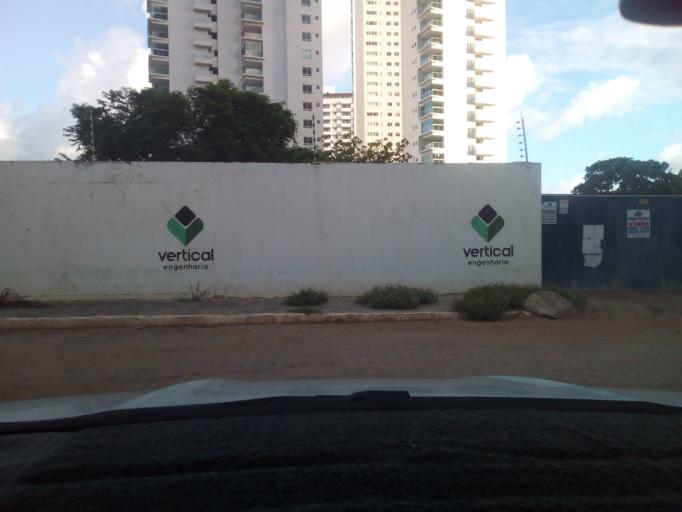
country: BR
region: Paraiba
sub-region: Joao Pessoa
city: Joao Pessoa
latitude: -7.1320
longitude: -34.8273
